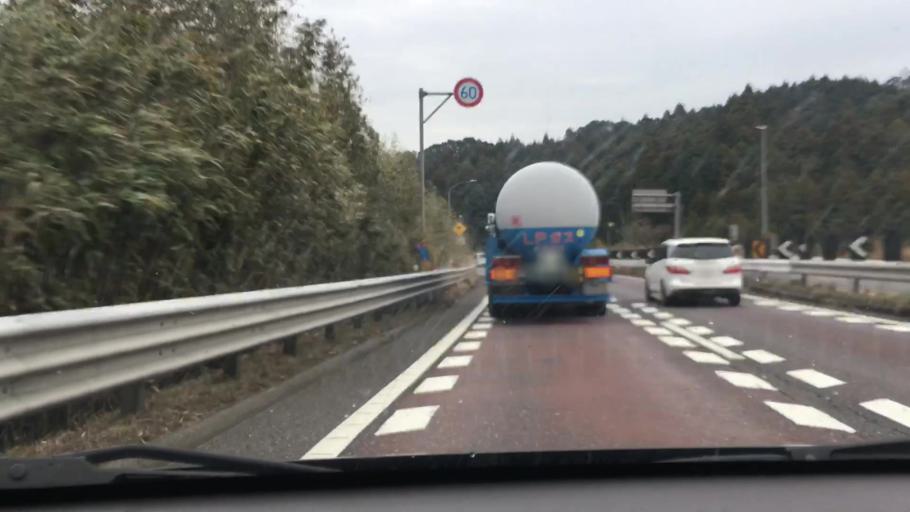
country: JP
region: Mie
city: Kameyama
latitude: 34.8391
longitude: 136.3769
